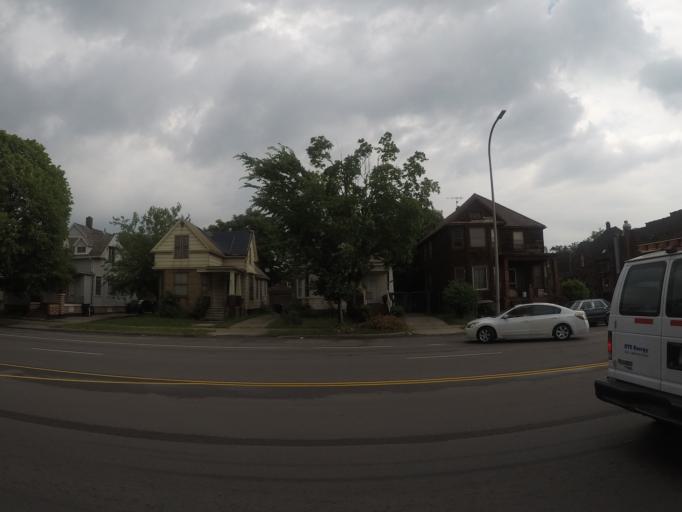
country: US
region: Michigan
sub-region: Wayne County
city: River Rouge
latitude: 42.3266
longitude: -83.1171
